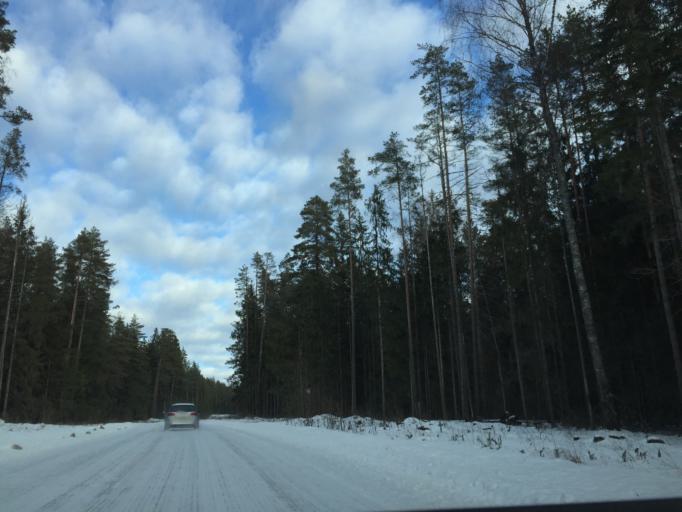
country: LV
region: Ogre
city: Jumprava
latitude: 56.5551
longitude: 24.9001
